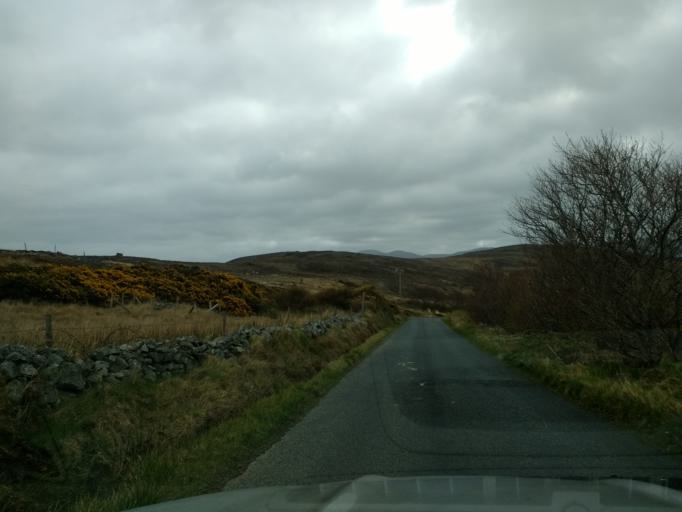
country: IE
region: Ulster
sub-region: County Donegal
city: Ramelton
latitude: 55.2619
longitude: -7.6374
